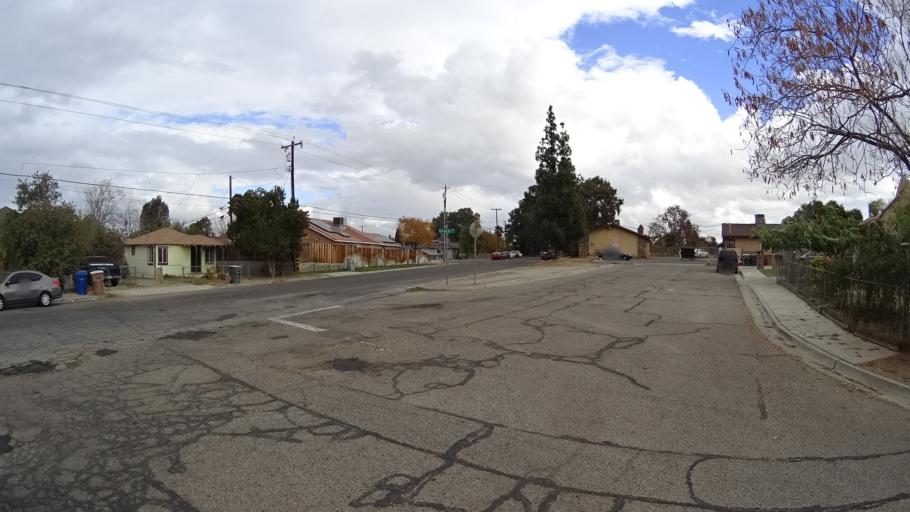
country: US
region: California
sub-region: Kern County
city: Bakersfield
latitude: 35.3910
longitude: -118.9811
